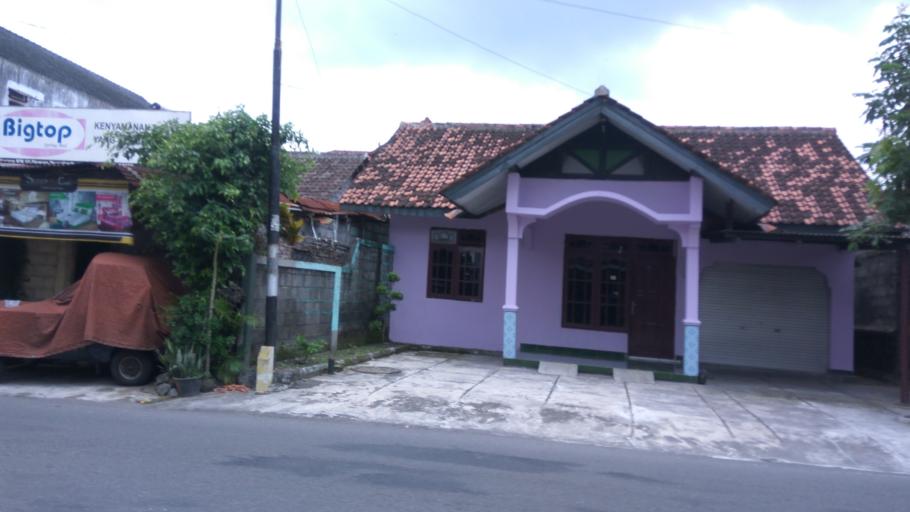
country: ID
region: Daerah Istimewa Yogyakarta
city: Melati
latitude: -7.7223
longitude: 110.4024
